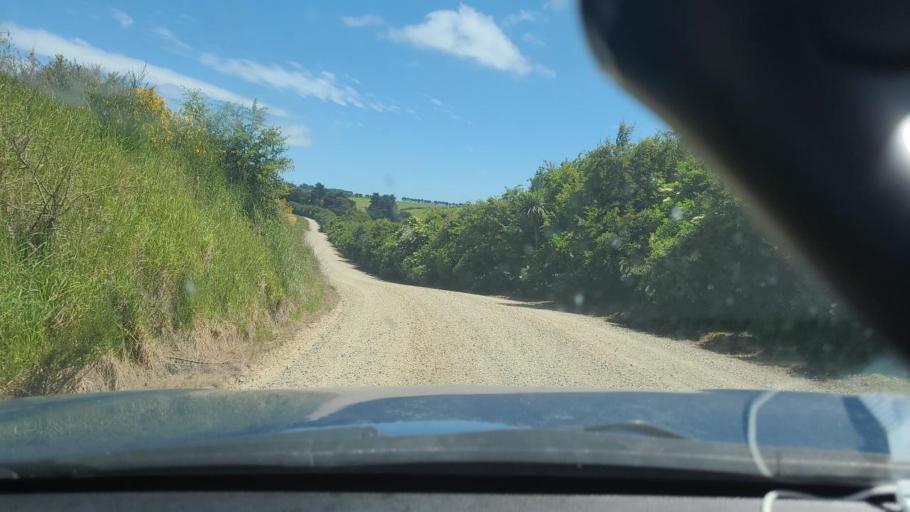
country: NZ
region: Southland
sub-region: Gore District
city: Gore
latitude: -46.3775
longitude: 168.9023
